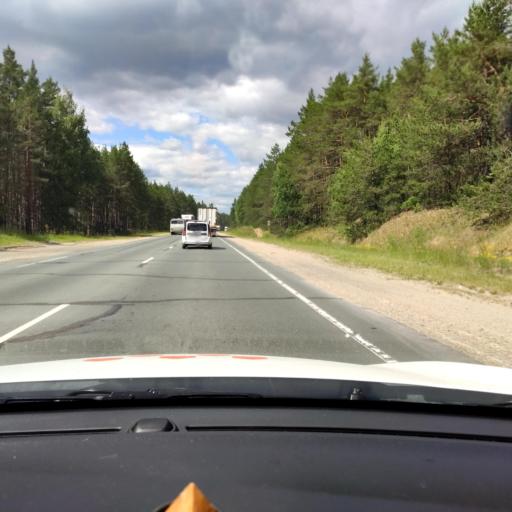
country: RU
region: Mariy-El
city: Krasnogorskiy
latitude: 56.0947
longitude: 48.3466
